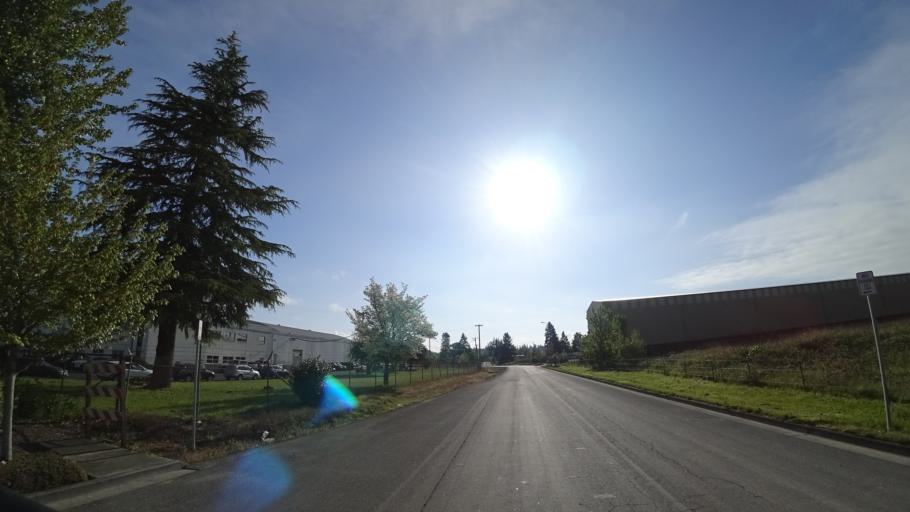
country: US
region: Oregon
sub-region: Washington County
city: Hillsboro
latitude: 45.5126
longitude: -122.9977
